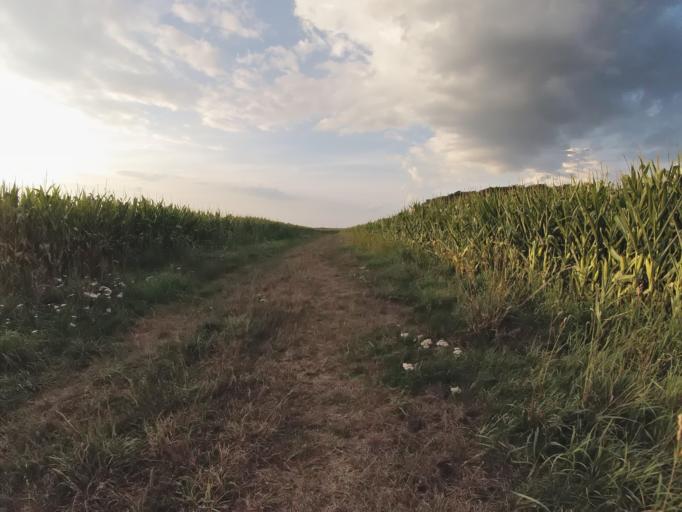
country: DE
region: North Rhine-Westphalia
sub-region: Regierungsbezirk Munster
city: Westerkappeln
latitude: 52.3474
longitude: 7.8887
